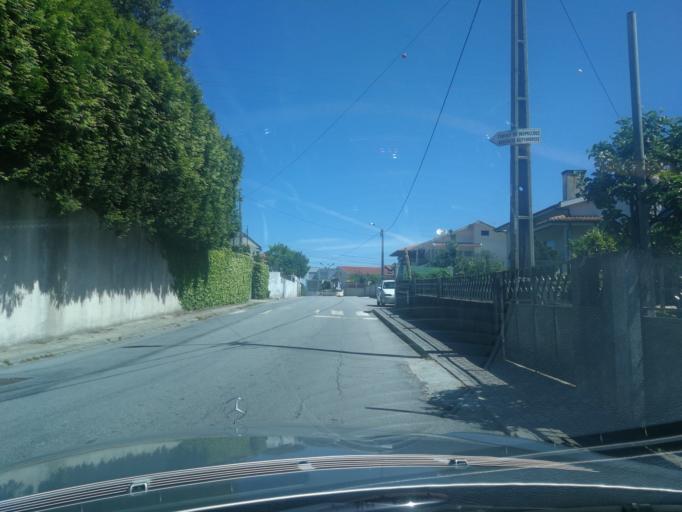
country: PT
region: Braga
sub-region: Braga
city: Adaufe
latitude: 41.5725
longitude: -8.4023
